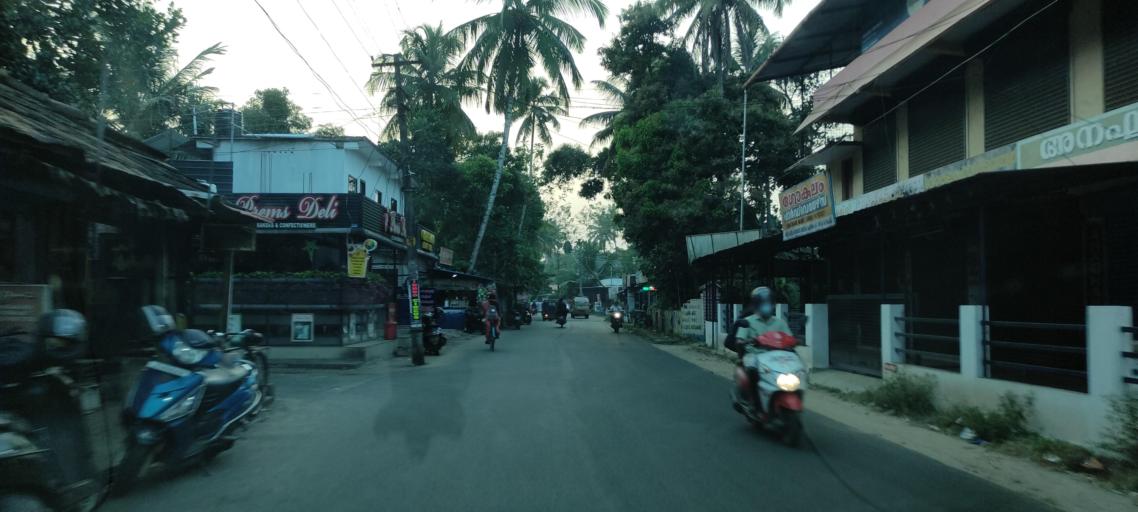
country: IN
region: Kerala
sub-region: Alappuzha
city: Kayankulam
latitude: 9.1335
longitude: 76.5083
